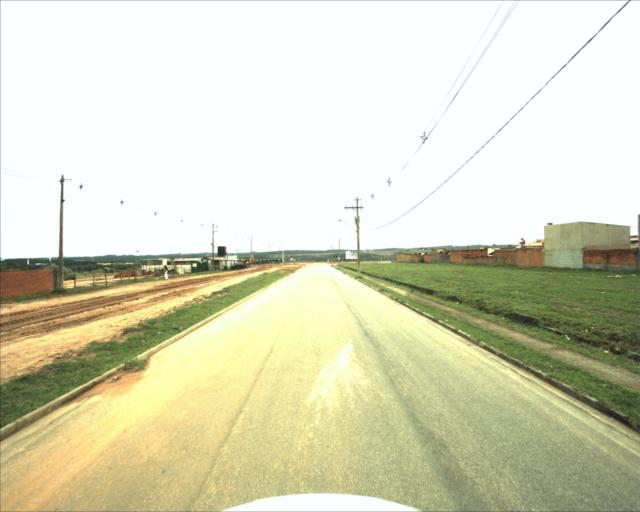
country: BR
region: Sao Paulo
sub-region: Sorocaba
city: Sorocaba
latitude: -23.4236
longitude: -47.4685
